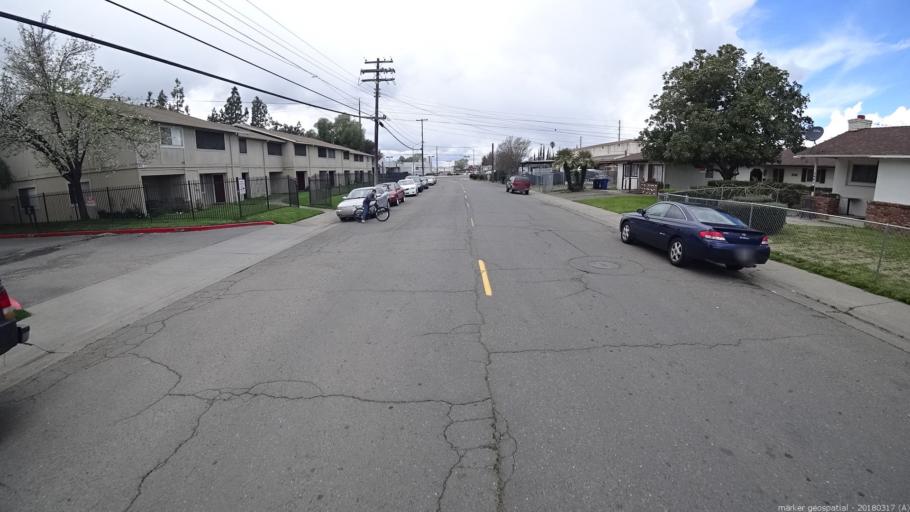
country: US
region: California
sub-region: Sacramento County
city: Parkway
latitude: 38.5045
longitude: -121.4626
